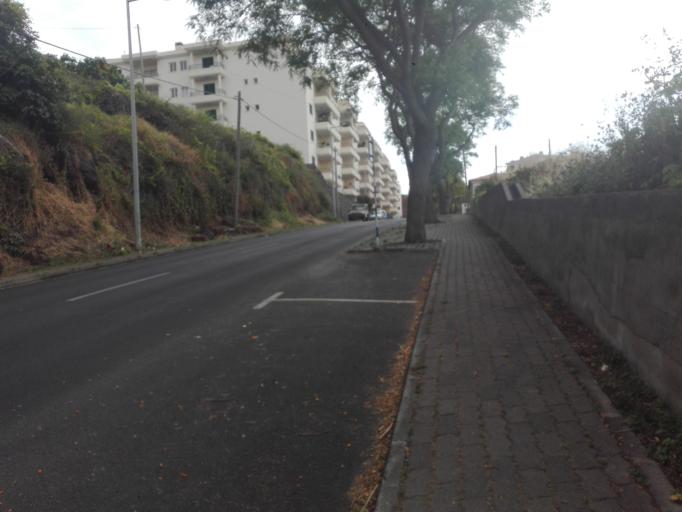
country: PT
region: Madeira
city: Canico
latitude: 32.6484
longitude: -16.8272
